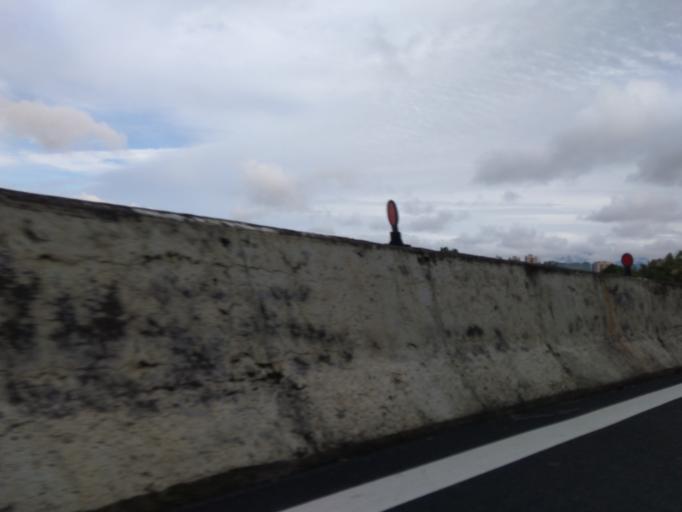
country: TW
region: Taiwan
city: Daxi
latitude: 24.9266
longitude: 121.1967
